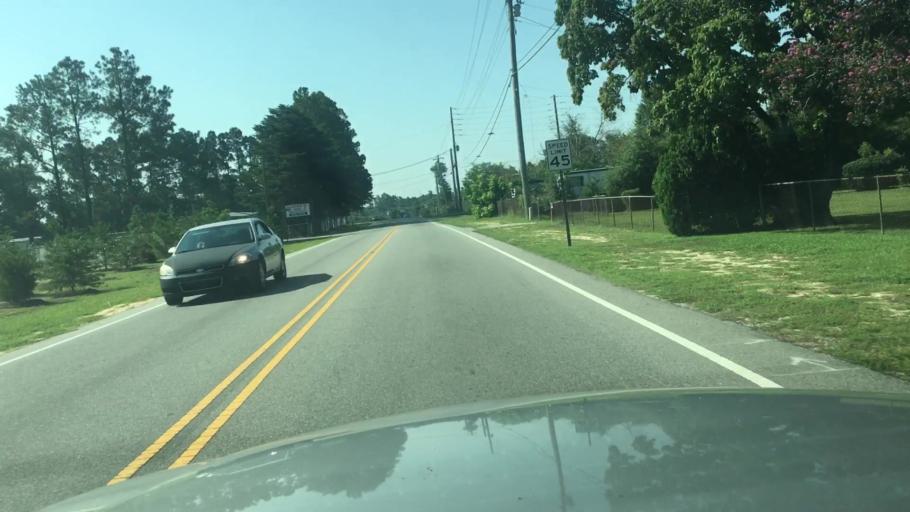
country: US
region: North Carolina
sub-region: Cumberland County
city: Spring Lake
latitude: 35.1472
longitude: -78.9111
